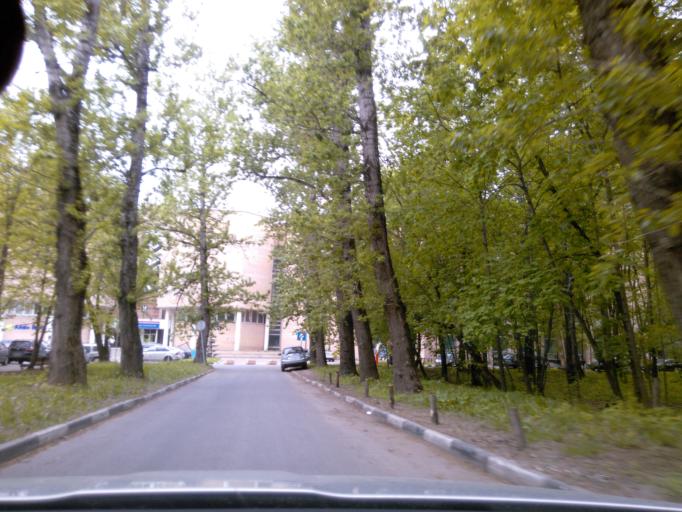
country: RU
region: Moskovskaya
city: Levoberezhnyy
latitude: 55.8582
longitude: 37.4675
